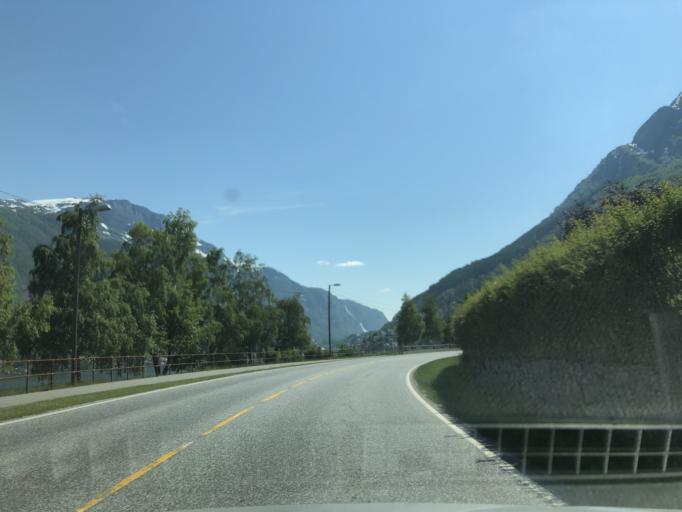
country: NO
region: Hordaland
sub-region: Odda
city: Odda
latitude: 60.0860
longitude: 6.5308
